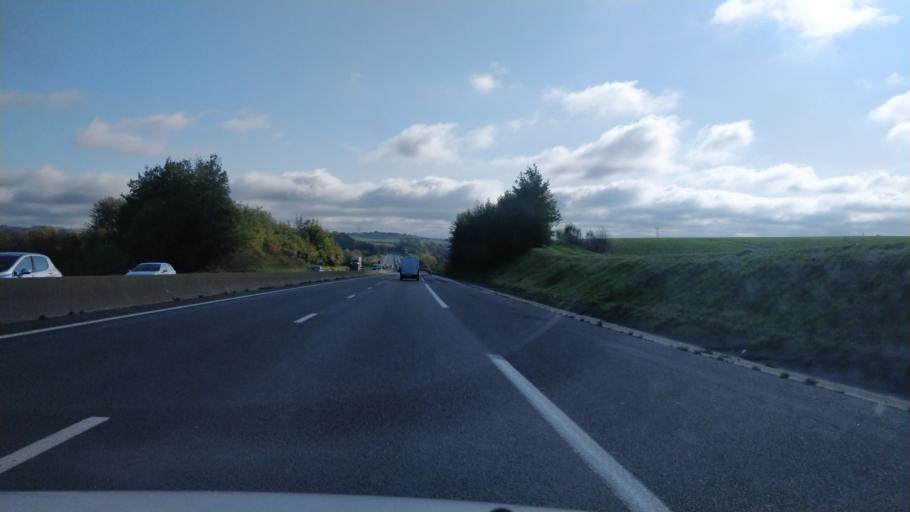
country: FR
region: Lower Normandy
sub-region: Departement du Calvados
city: Louvigny
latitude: 49.1436
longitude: -0.4044
